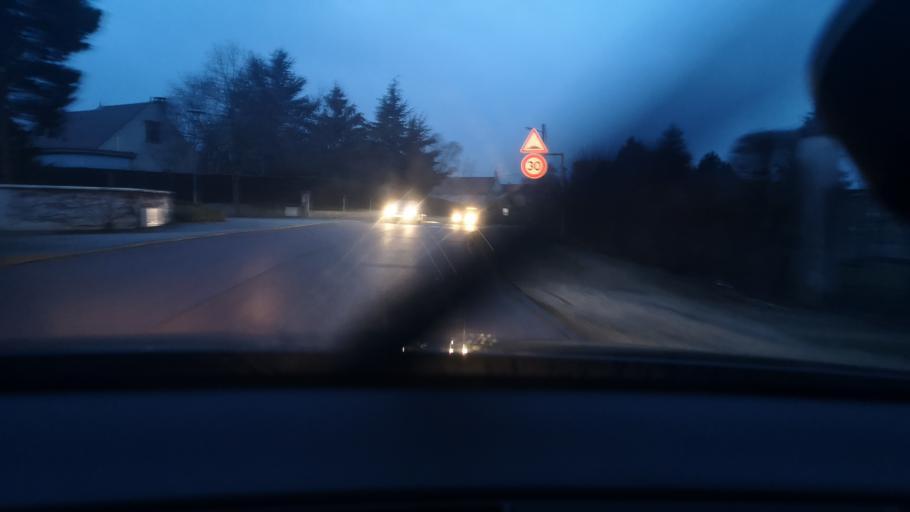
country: FR
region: Bourgogne
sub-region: Departement de Saone-et-Loire
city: Demigny
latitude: 46.9292
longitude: 4.8407
